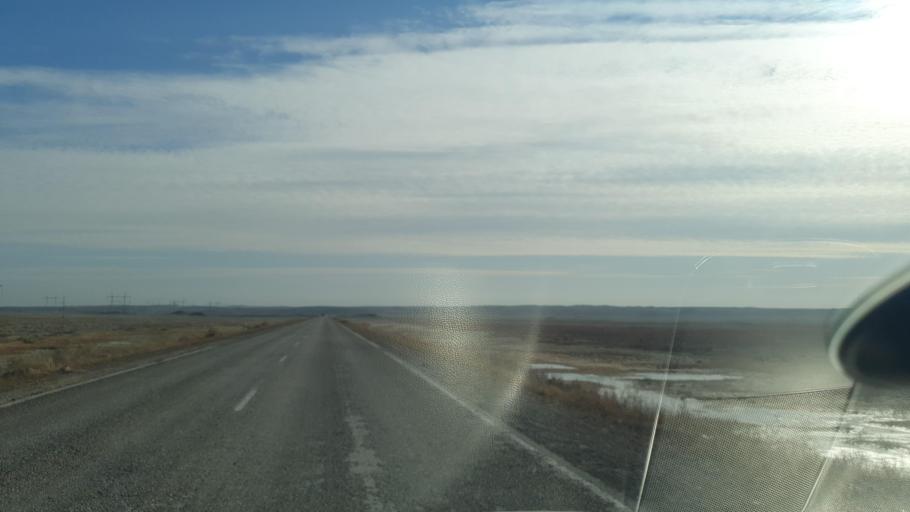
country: KZ
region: Zhambyl
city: Mynaral
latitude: 45.5757
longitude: 73.4131
